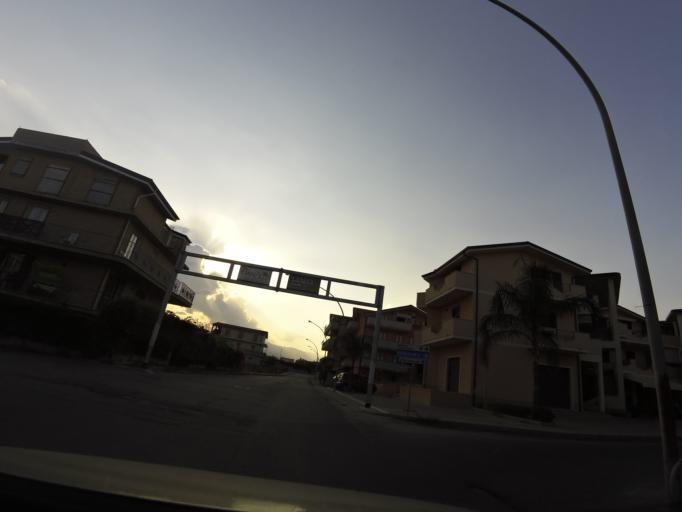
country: IT
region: Calabria
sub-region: Provincia di Reggio Calabria
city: Monasterace Marina
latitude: 38.4330
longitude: 16.5714
